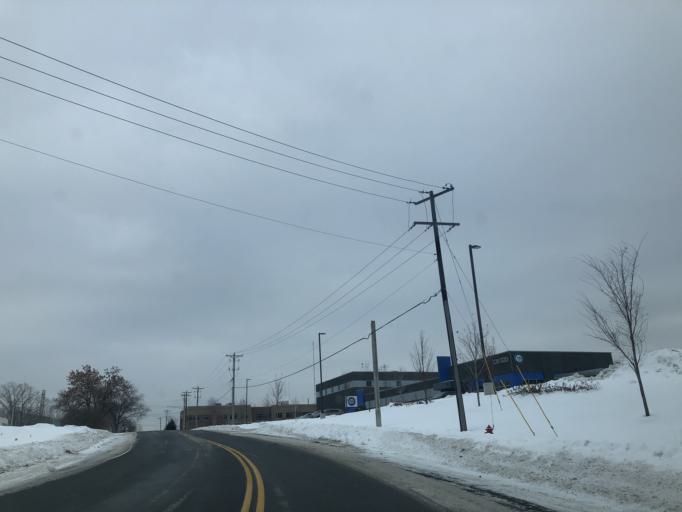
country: US
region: Minnesota
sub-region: Ramsey County
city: New Brighton
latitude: 45.0718
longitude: -93.1906
